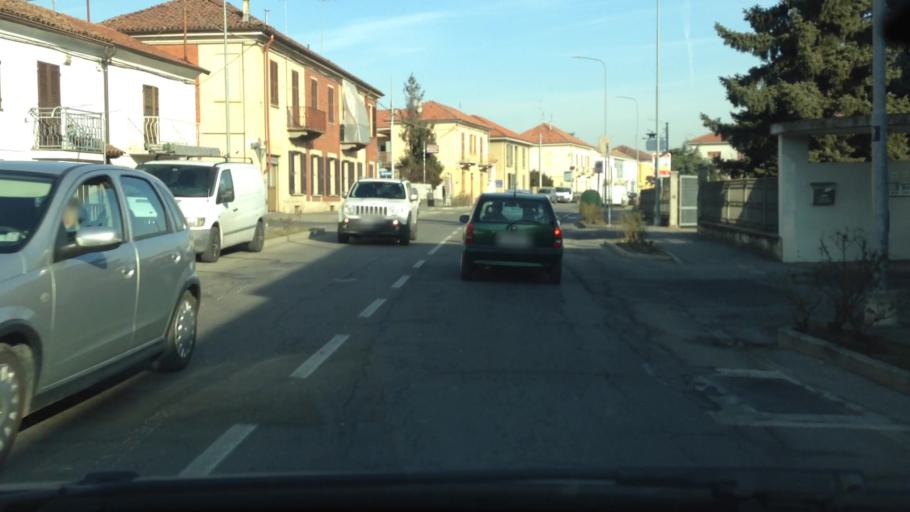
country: IT
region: Piedmont
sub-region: Provincia di Asti
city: Asti
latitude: 44.9122
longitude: 8.2198
